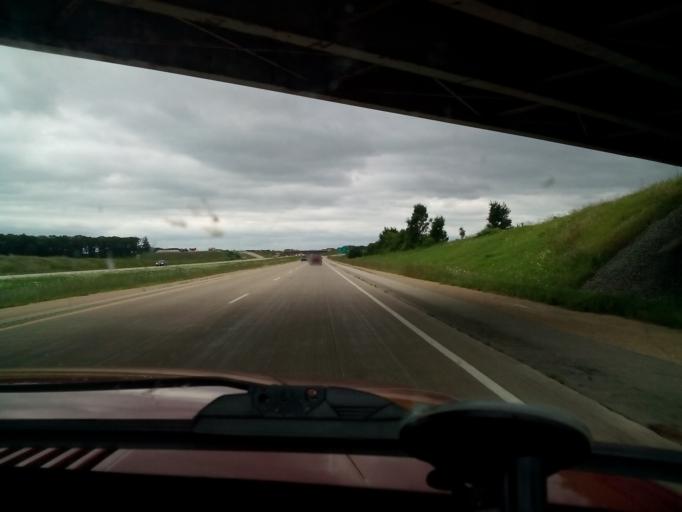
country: US
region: Wisconsin
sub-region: Columbia County
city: Columbus
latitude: 43.3264
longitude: -89.0452
